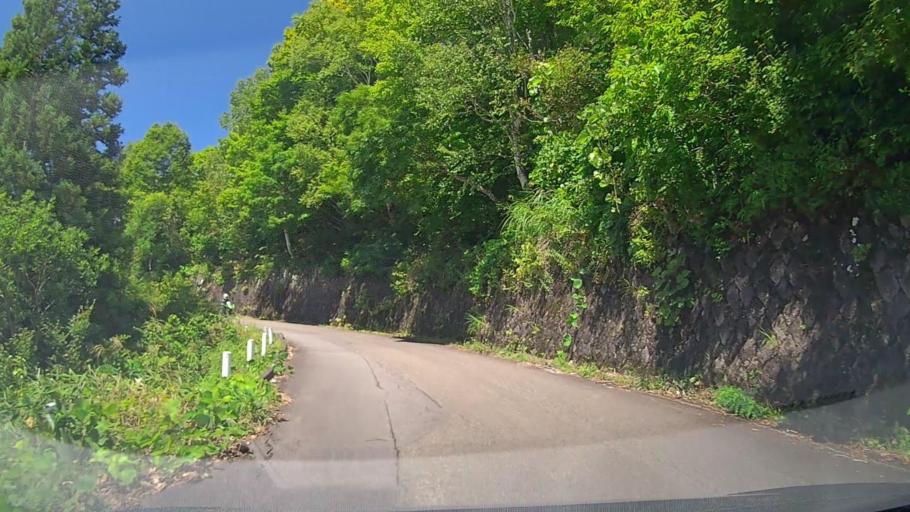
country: JP
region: Nagano
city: Iiyama
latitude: 36.9341
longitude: 138.4538
